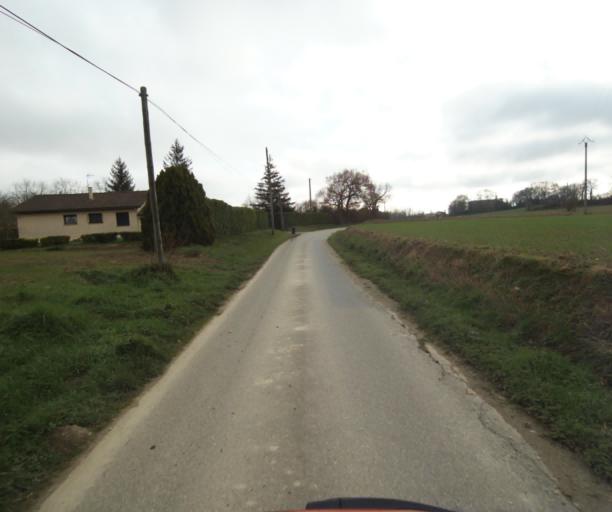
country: FR
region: Languedoc-Roussillon
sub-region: Departement de l'Aude
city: Belpech
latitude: 43.1805
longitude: 1.7342
